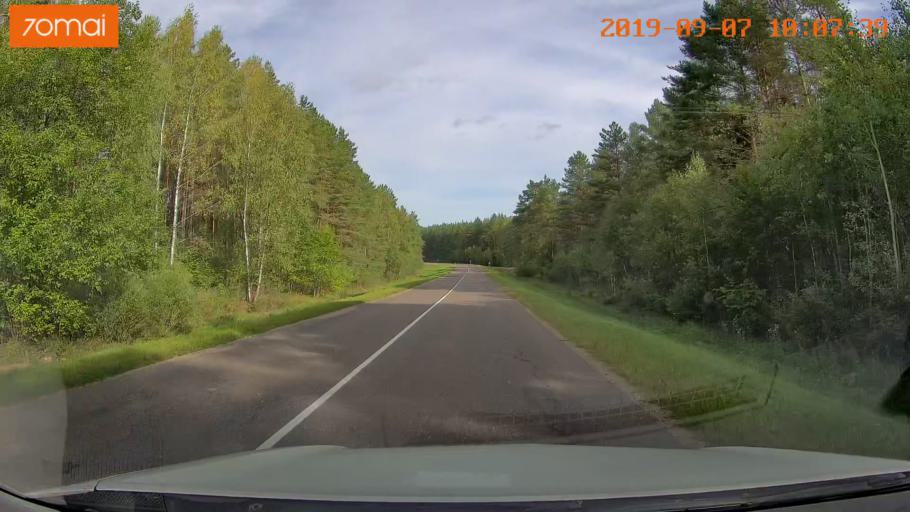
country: BY
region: Grodnenskaya
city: Voranava
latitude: 54.0783
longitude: 25.3958
